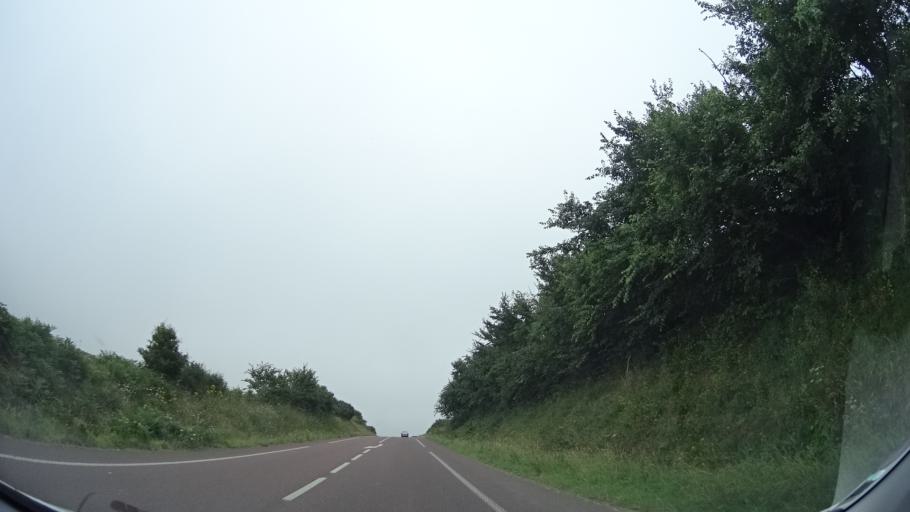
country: FR
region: Lower Normandy
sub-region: Departement de la Manche
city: Flamanville
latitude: 49.5494
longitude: -1.8549
